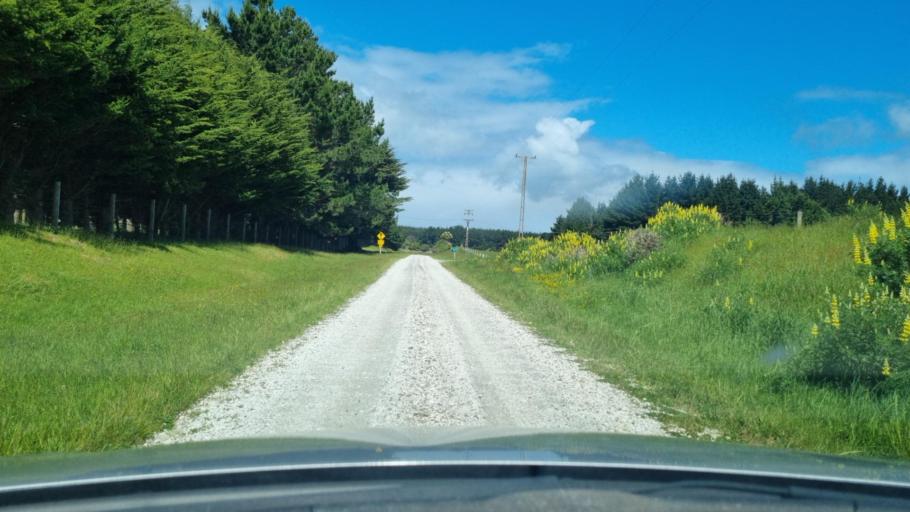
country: NZ
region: Southland
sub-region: Invercargill City
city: Invercargill
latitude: -46.4573
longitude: 168.2719
